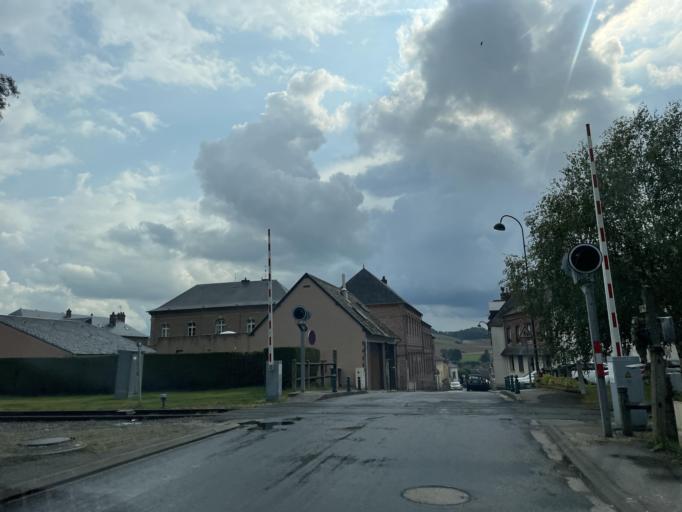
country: FR
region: Haute-Normandie
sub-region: Departement de la Seine-Maritime
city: Envermeu
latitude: 49.8977
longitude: 1.2648
